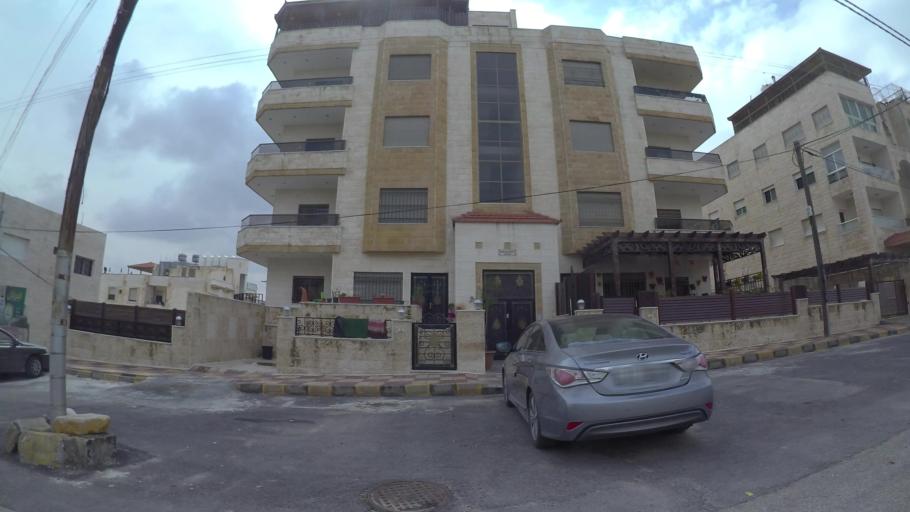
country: JO
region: Amman
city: Umm as Summaq
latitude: 31.8963
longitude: 35.8367
